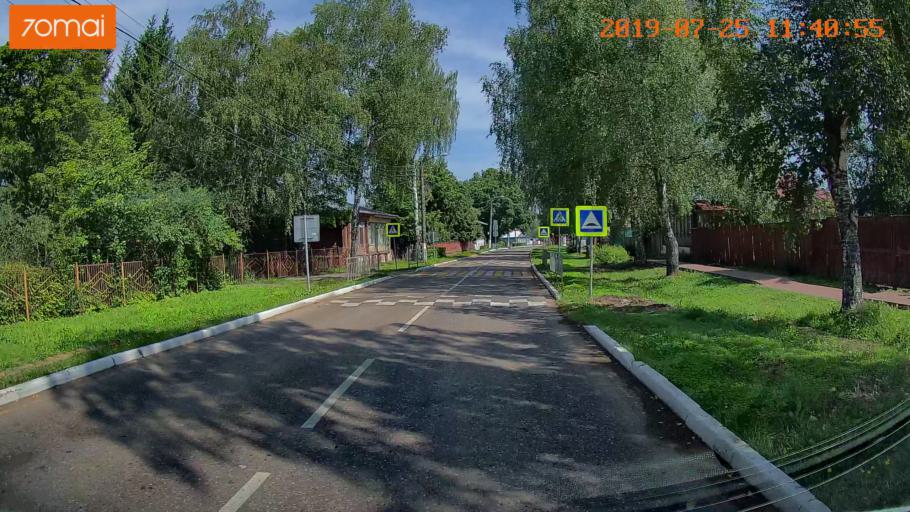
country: RU
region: Ivanovo
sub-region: Privolzhskiy Rayon
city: Ples
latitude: 57.4554
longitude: 41.5105
